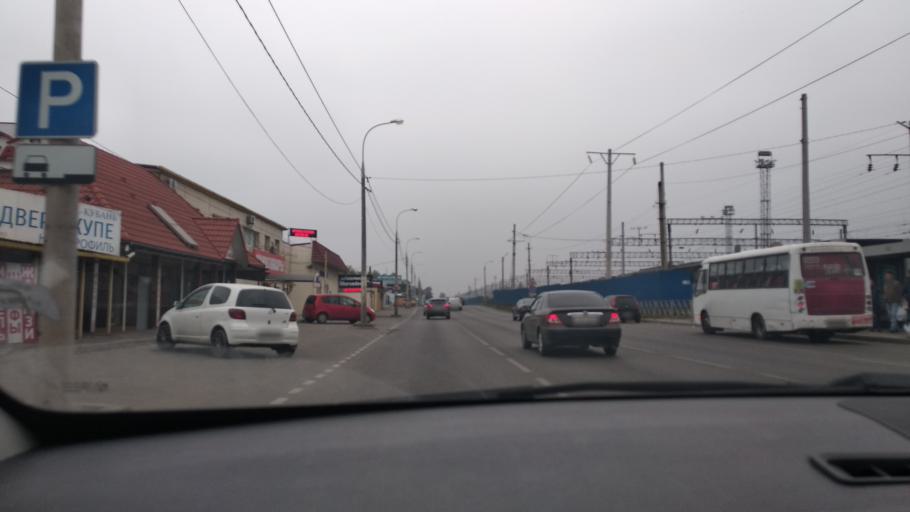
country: RU
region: Krasnodarskiy
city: Pashkovskiy
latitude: 45.0372
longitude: 39.0505
